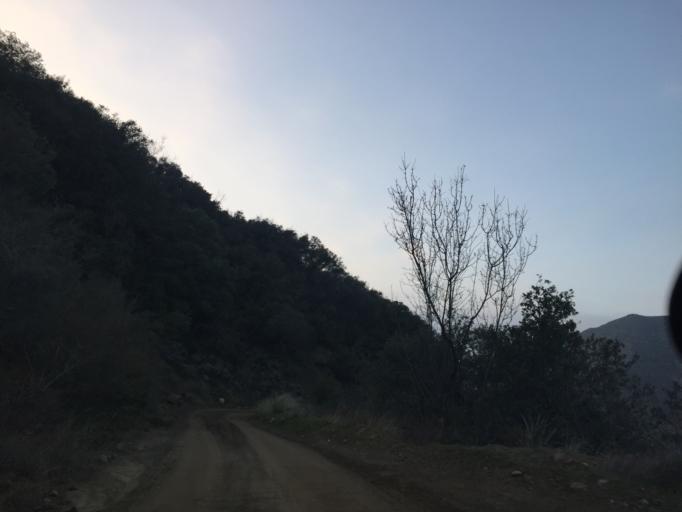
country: US
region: California
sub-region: San Bernardino County
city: Yucaipa
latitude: 34.1134
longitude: -117.0441
